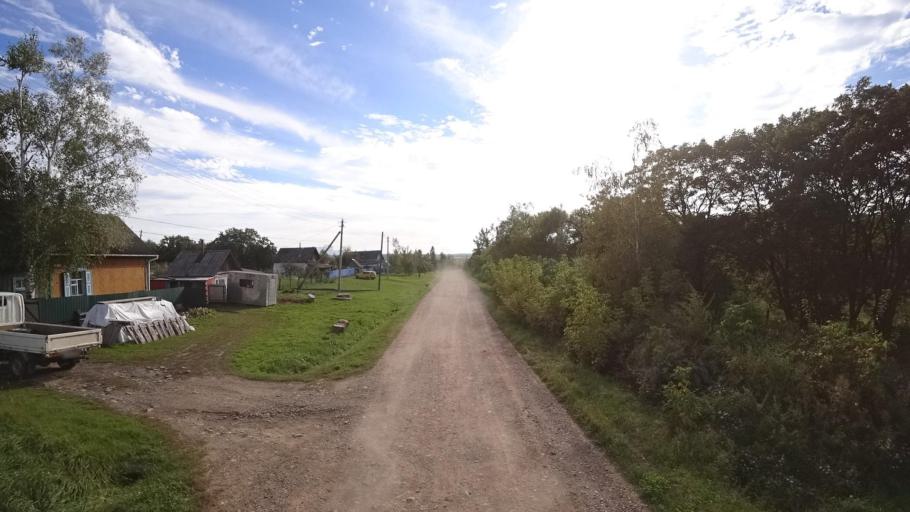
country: RU
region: Primorskiy
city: Dostoyevka
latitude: 44.2979
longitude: 133.4512
